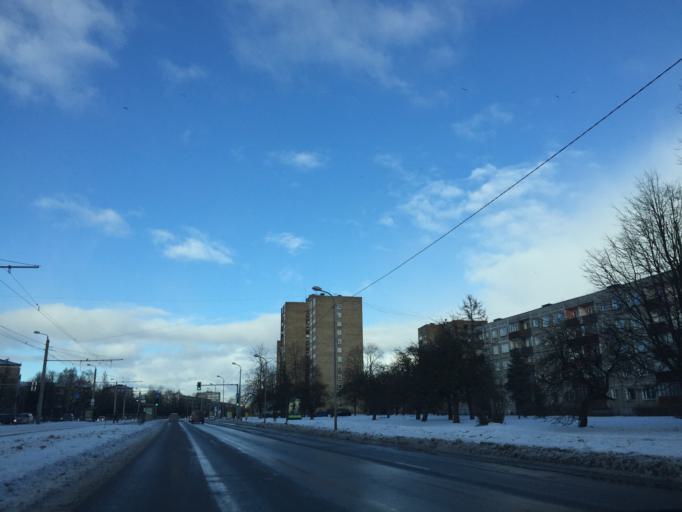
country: LV
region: Kekava
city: Balozi
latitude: 56.9115
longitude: 24.1784
